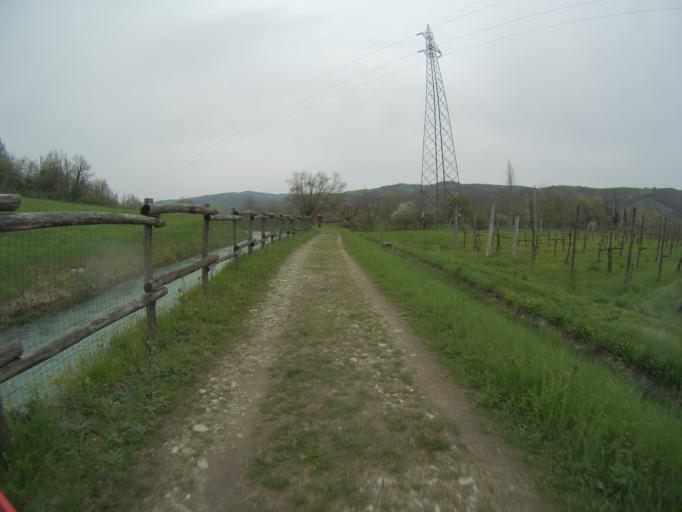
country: IT
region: Emilia-Romagna
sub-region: Provincia di Reggio Emilia
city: Ciano d'Enza
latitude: 44.6026
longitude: 10.4050
